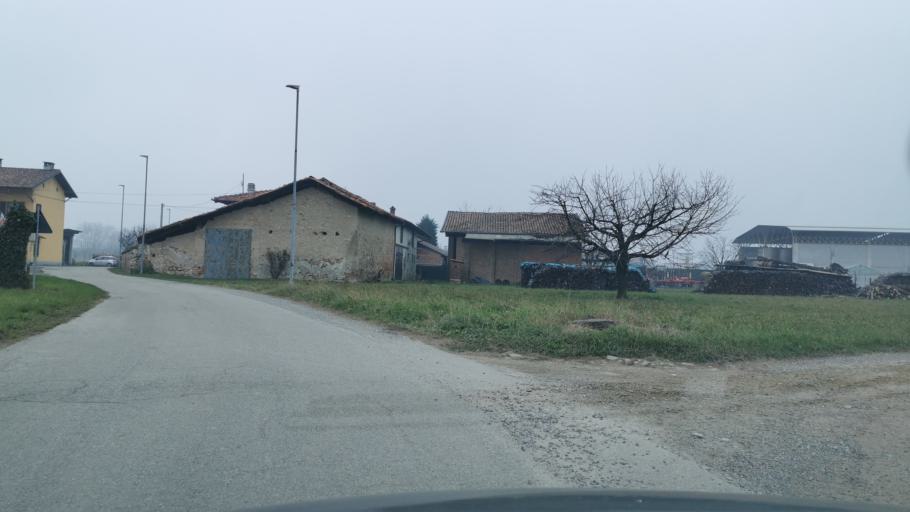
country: IT
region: Piedmont
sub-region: Provincia di Torino
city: Rivara
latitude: 45.3251
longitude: 7.6448
